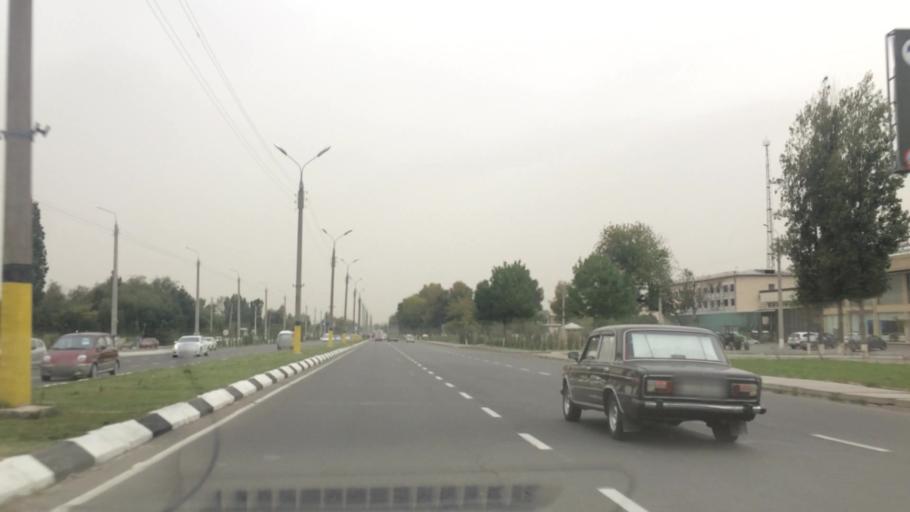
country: UZ
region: Toshkent
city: Salor
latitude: 41.3153
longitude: 69.3535
